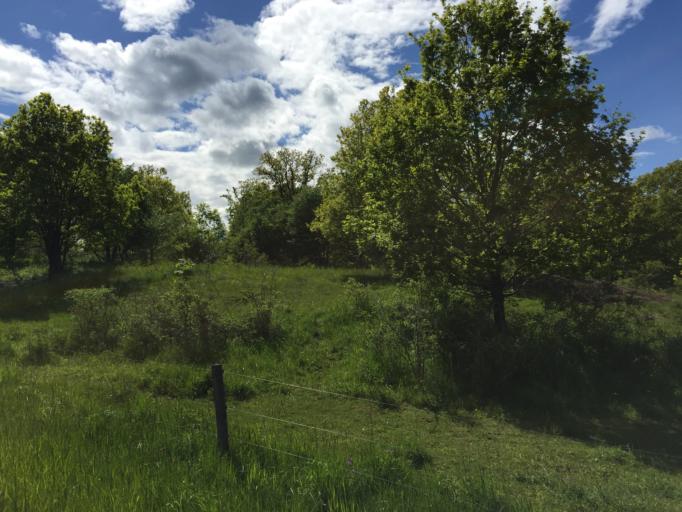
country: SE
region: OEstergoetland
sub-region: Norrkopings Kommun
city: Kimstad
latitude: 58.5215
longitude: 15.9719
